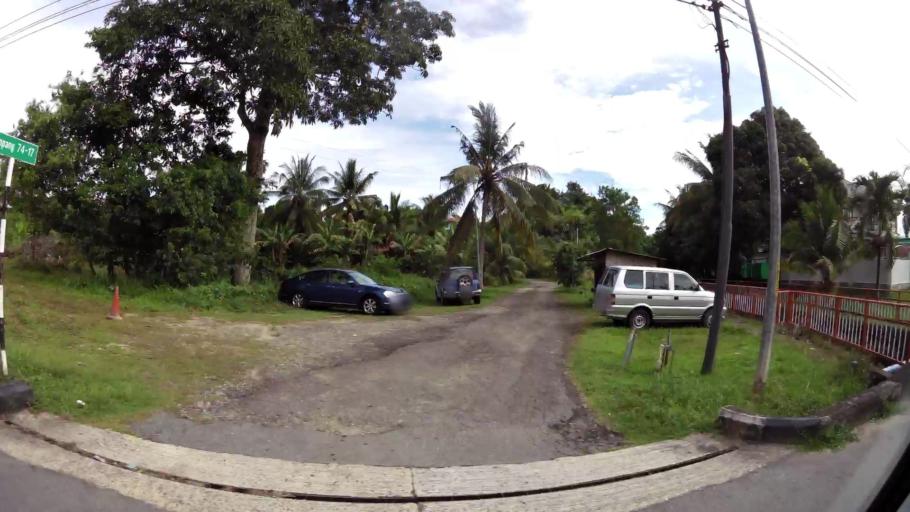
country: BN
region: Brunei and Muara
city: Bandar Seri Begawan
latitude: 4.8998
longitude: 114.8946
